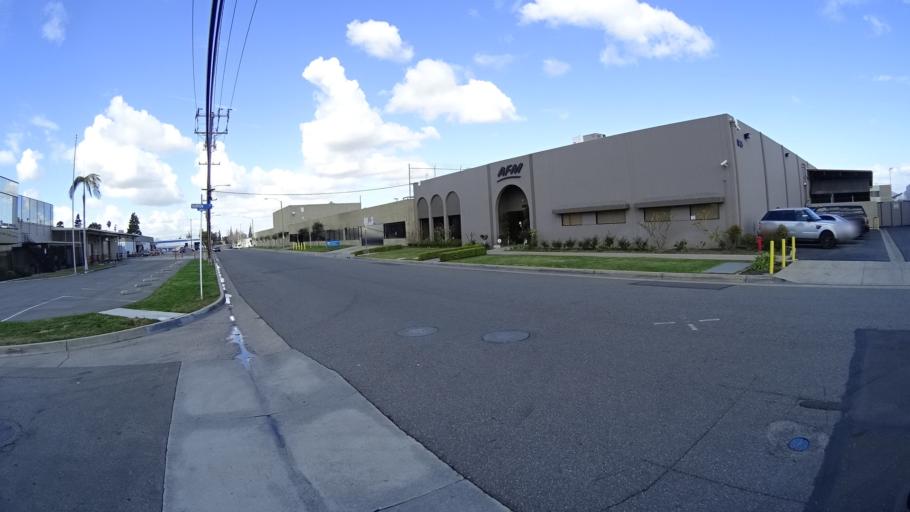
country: US
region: California
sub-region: Orange County
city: Placentia
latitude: 33.8563
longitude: -117.8916
